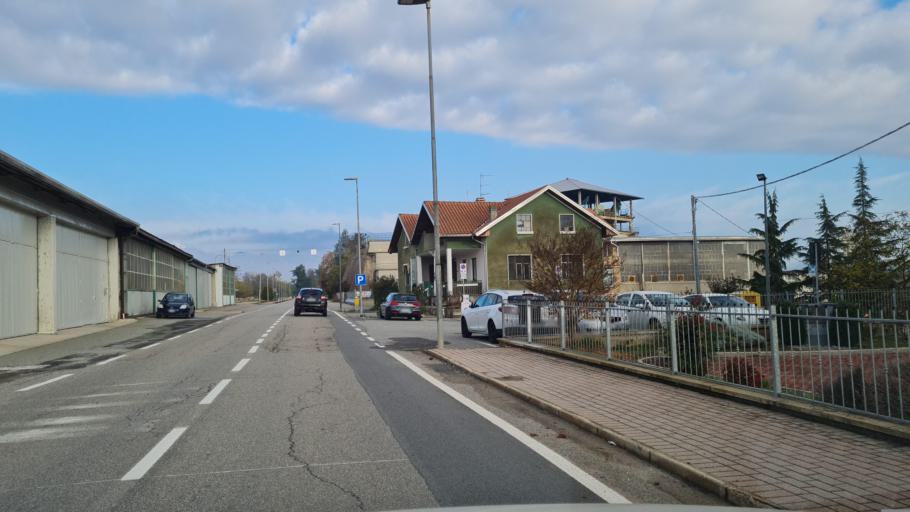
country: IT
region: Piedmont
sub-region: Provincia di Biella
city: Castelletto Cervo
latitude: 45.5190
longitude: 8.2249
